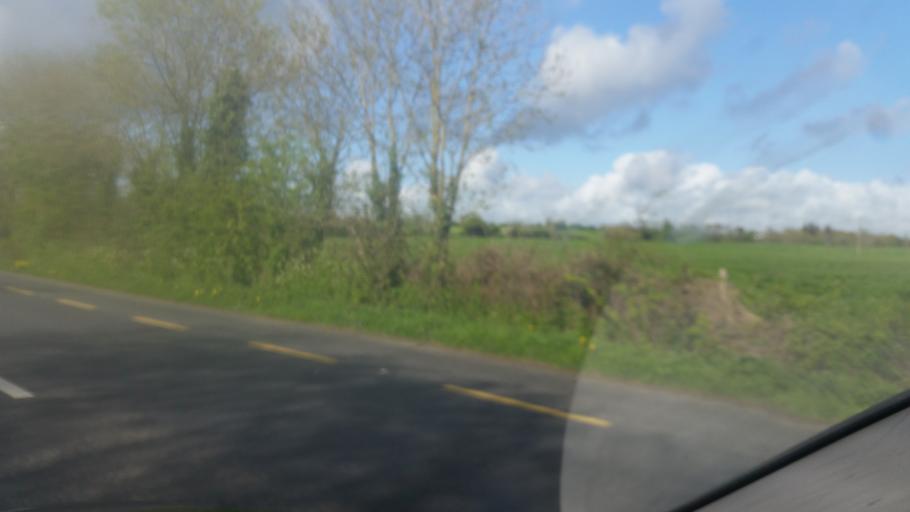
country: IE
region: Leinster
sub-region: Loch Garman
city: Ferns
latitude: 52.5609
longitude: -6.5306
